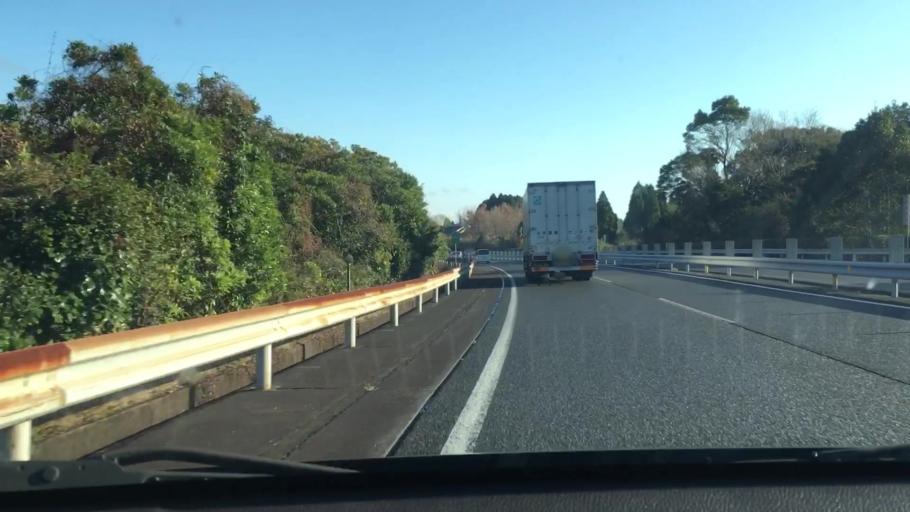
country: JP
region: Kagoshima
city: Kajiki
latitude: 31.8224
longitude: 130.6946
